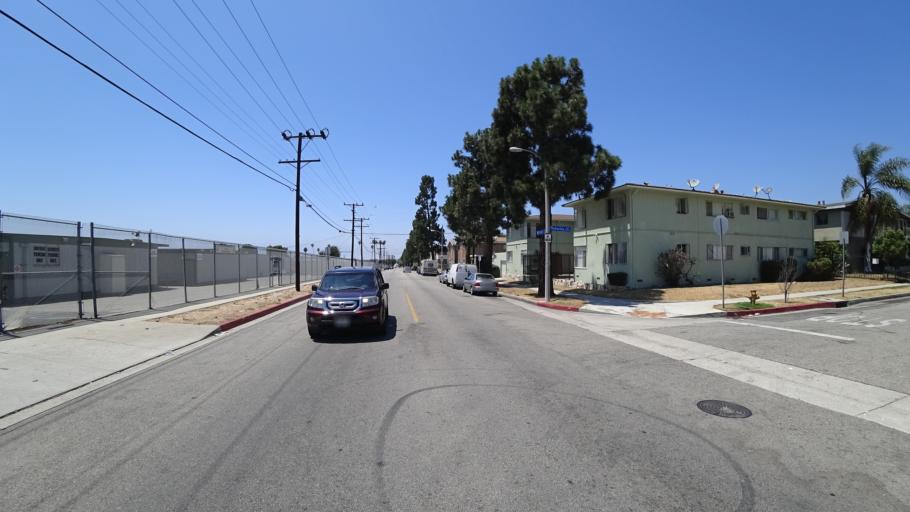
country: US
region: California
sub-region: Los Angeles County
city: Lennox
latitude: 33.9418
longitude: -118.3309
